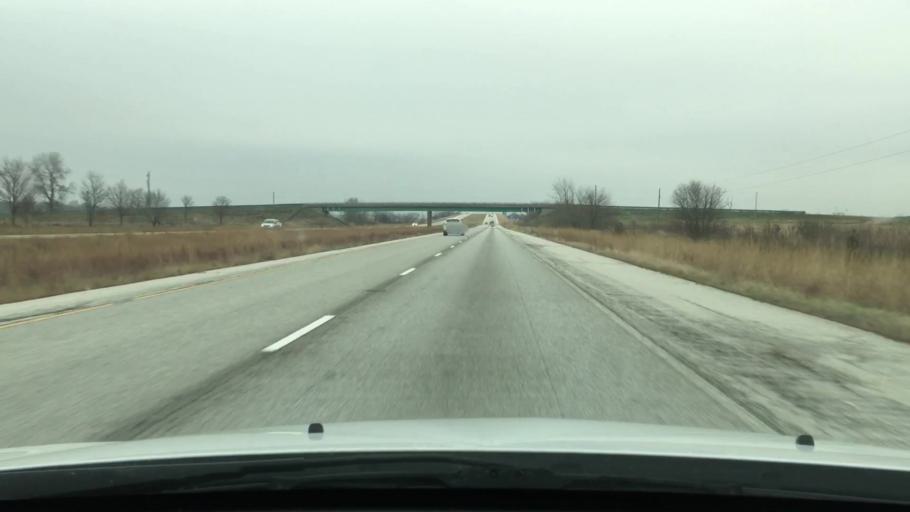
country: US
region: Illinois
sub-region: Morgan County
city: South Jacksonville
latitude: 39.6998
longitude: -90.1909
